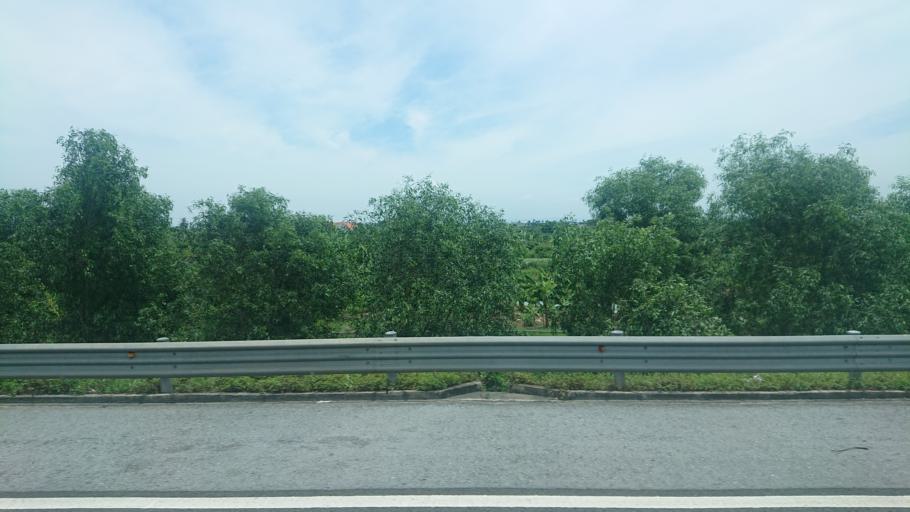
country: VN
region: Hai Duong
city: Tu Ky
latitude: 20.8197
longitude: 106.4803
